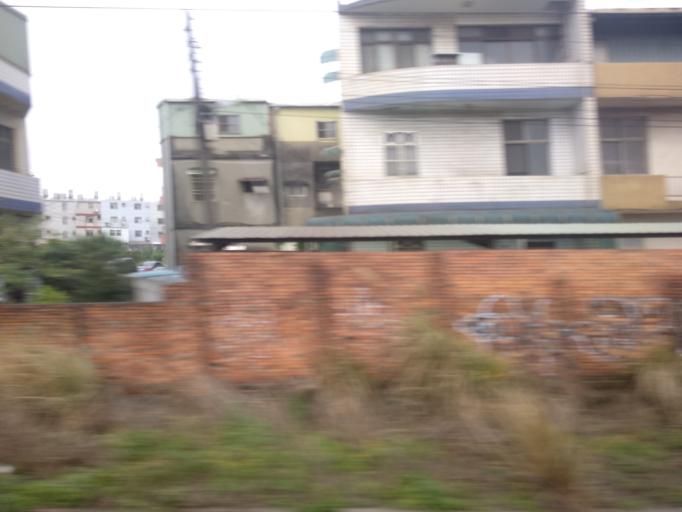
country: TW
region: Taiwan
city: Daxi
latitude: 24.9367
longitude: 121.2085
